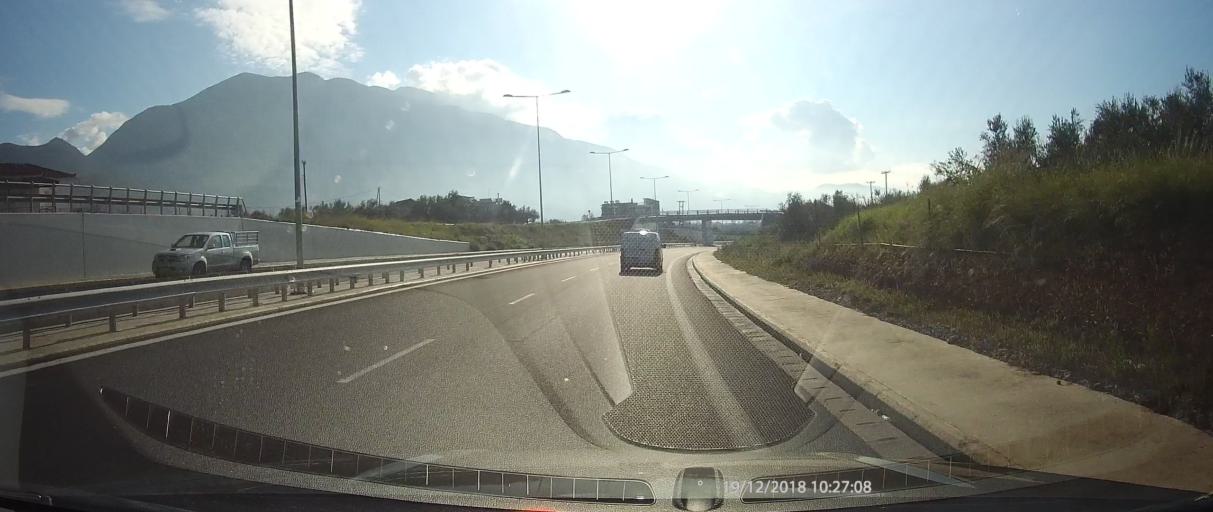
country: GR
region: Peloponnese
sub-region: Nomos Messinias
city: Kalamata
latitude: 37.0397
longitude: 22.1345
